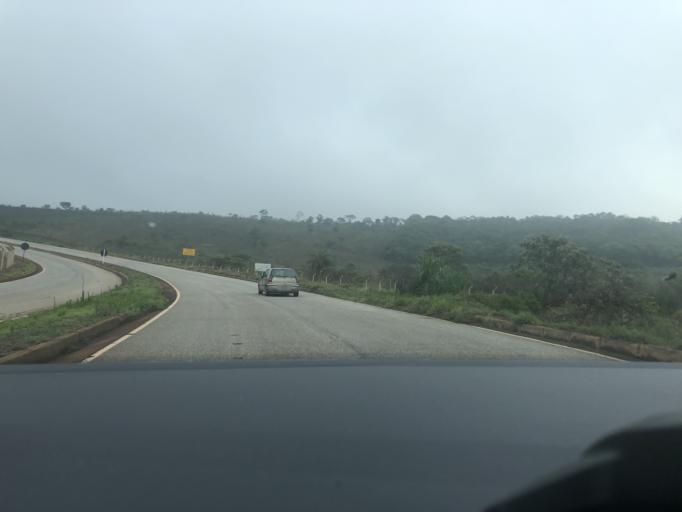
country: BR
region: Minas Gerais
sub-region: Congonhas
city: Congonhas
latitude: -20.5888
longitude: -43.9467
